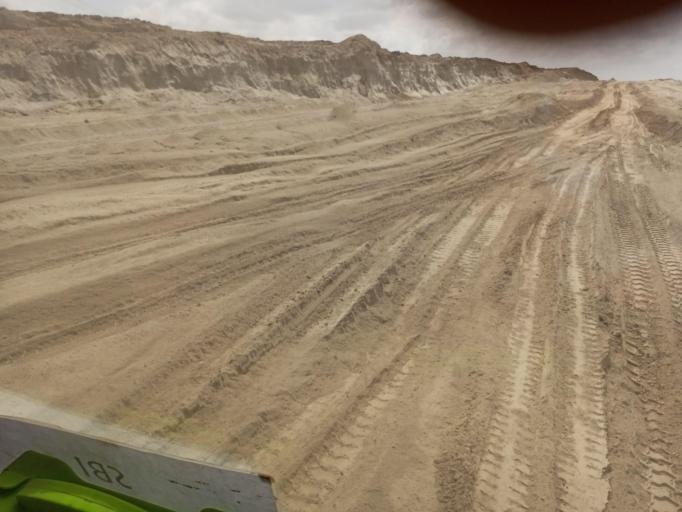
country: ET
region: Oromiya
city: Shashemene
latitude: 7.4814
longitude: 38.6811
